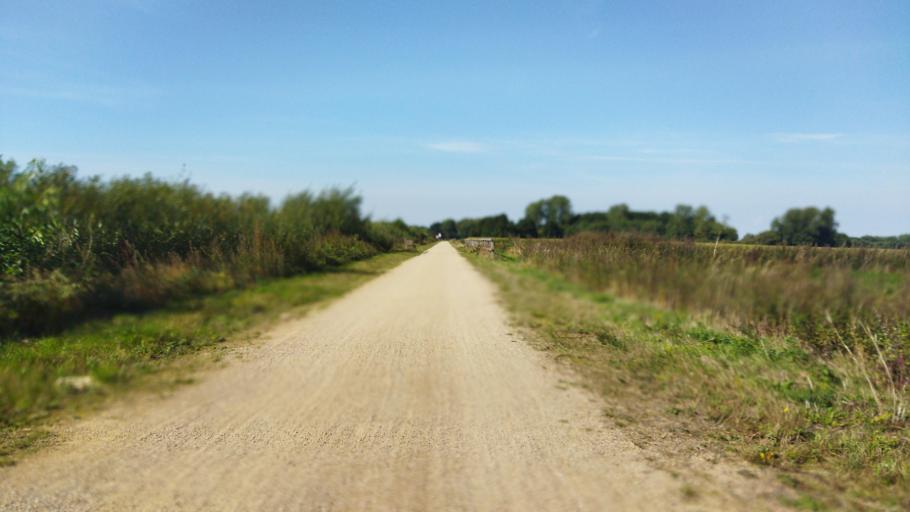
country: DE
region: Lower Saxony
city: Haren
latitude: 52.7780
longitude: 7.2694
